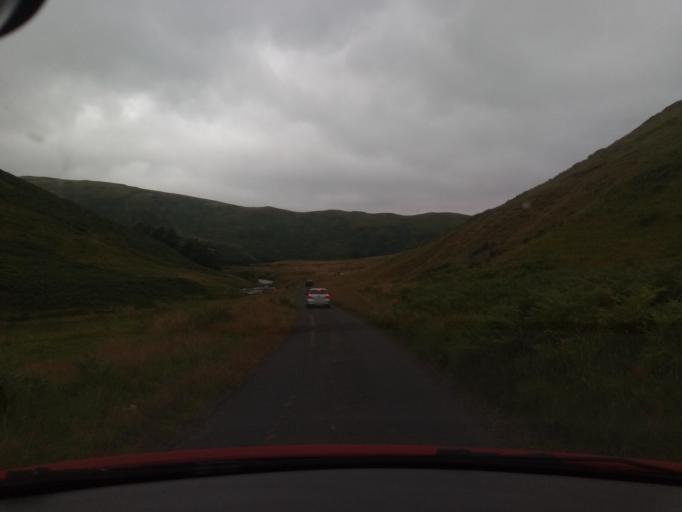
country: GB
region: England
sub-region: Northumberland
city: Rochester
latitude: 55.3604
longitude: -2.1782
